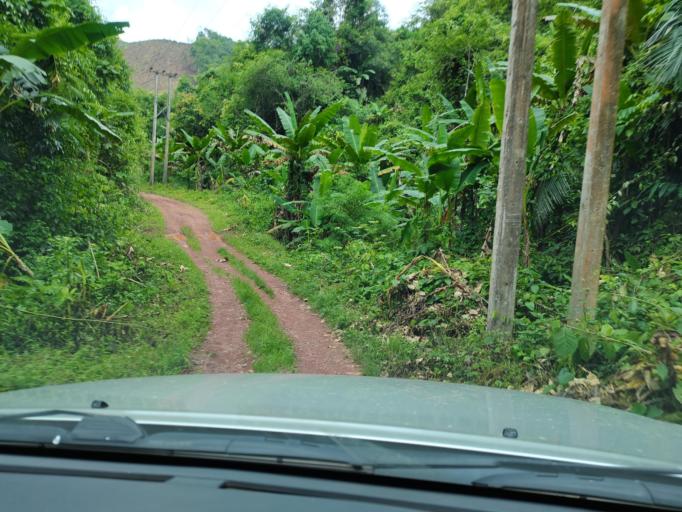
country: LA
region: Loungnamtha
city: Muang Nale
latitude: 20.5155
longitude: 101.0741
